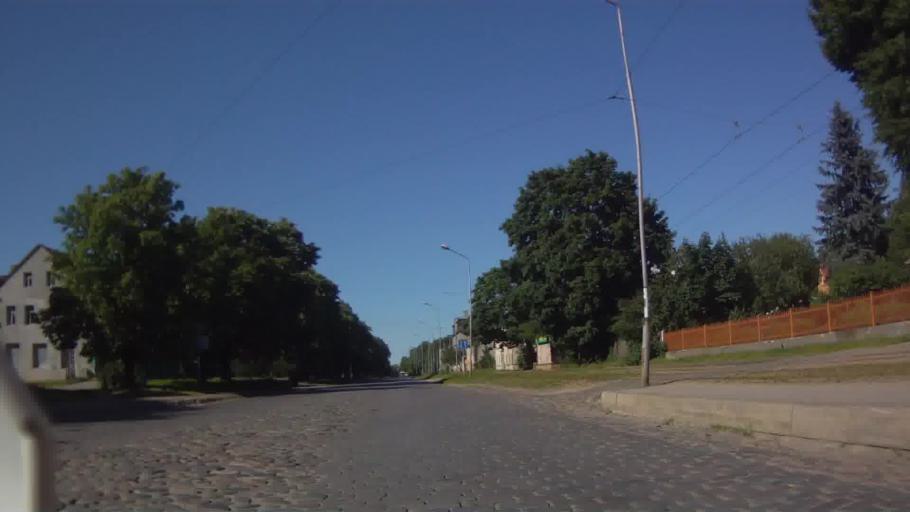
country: LV
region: Riga
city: Riga
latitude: 56.9240
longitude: 24.0897
